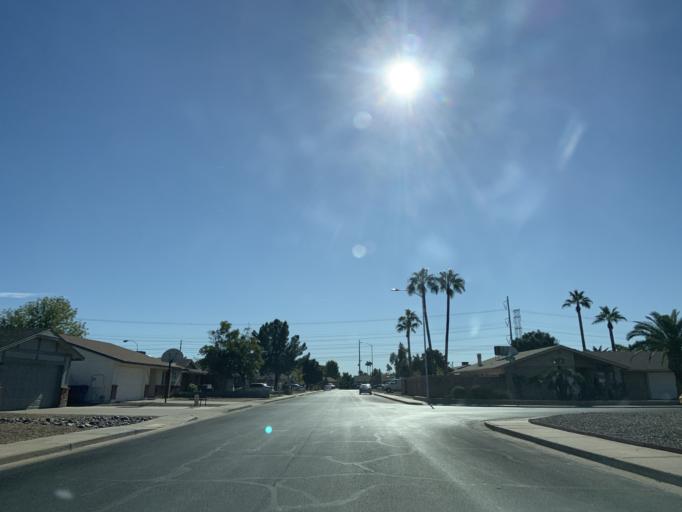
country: US
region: Arizona
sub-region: Maricopa County
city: San Carlos
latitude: 33.3591
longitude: -111.8639
